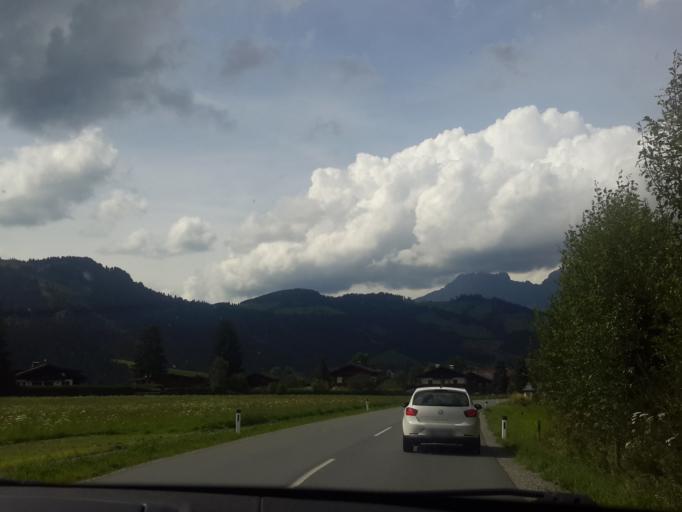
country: AT
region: Tyrol
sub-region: Politischer Bezirk Kitzbuhel
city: Reith bei Kitzbuhel
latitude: 47.4622
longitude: 12.3538
